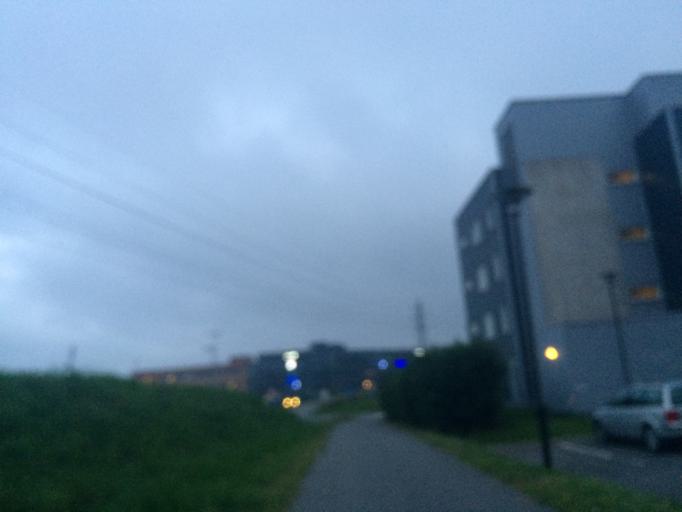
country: NO
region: Akershus
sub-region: Ski
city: Ski
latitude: 59.7160
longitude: 10.8311
